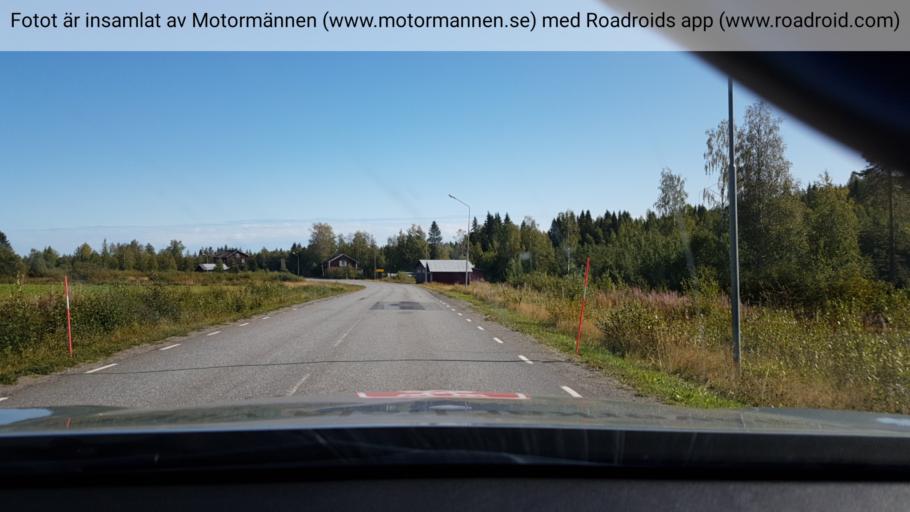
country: SE
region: Vaesterbotten
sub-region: Norsjo Kommun
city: Norsjoe
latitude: 64.9495
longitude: 19.3950
